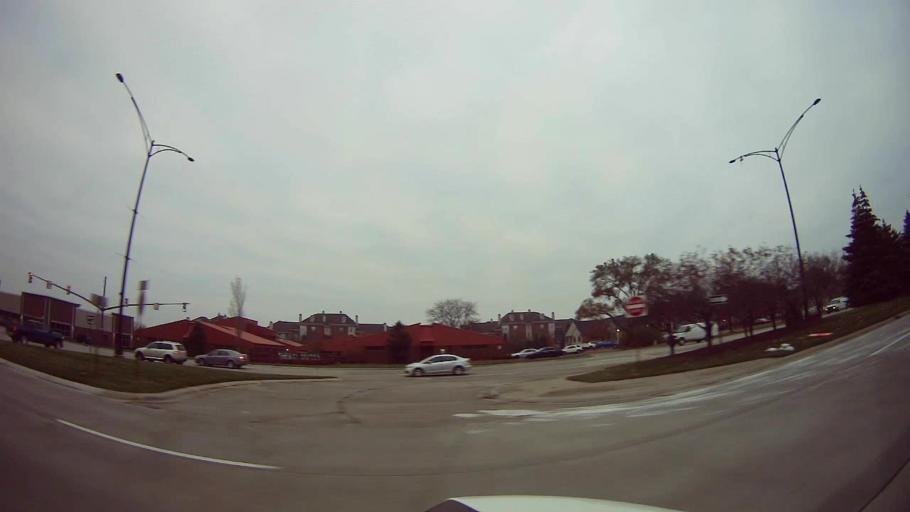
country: US
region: Michigan
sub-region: Oakland County
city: Clawson
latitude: 42.5619
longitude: -83.1702
